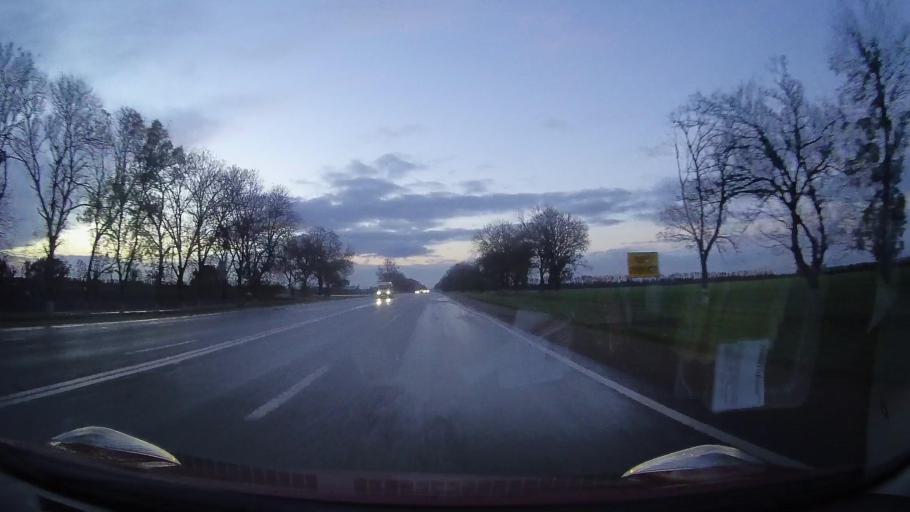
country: RU
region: Krasnodarskiy
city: Zavetnyy
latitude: 44.8864
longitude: 41.2162
